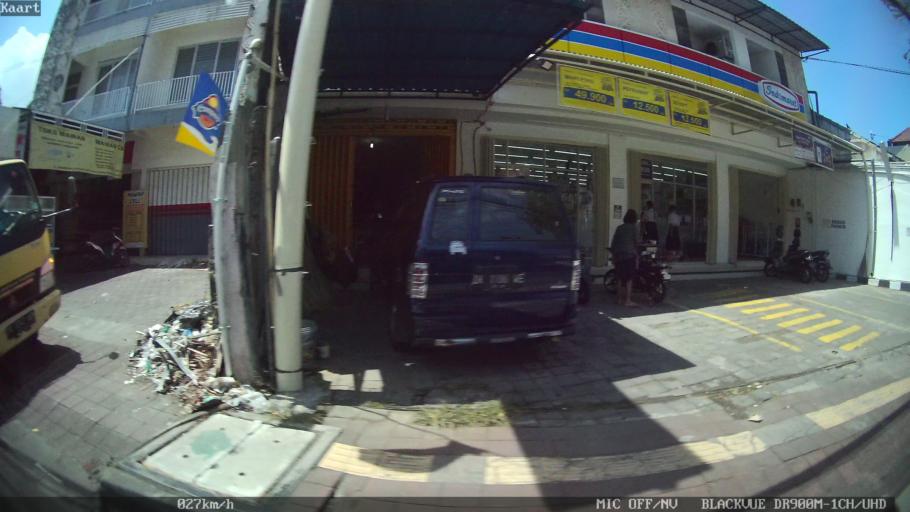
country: ID
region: Bali
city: Denpasar
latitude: -8.6657
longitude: 115.1987
